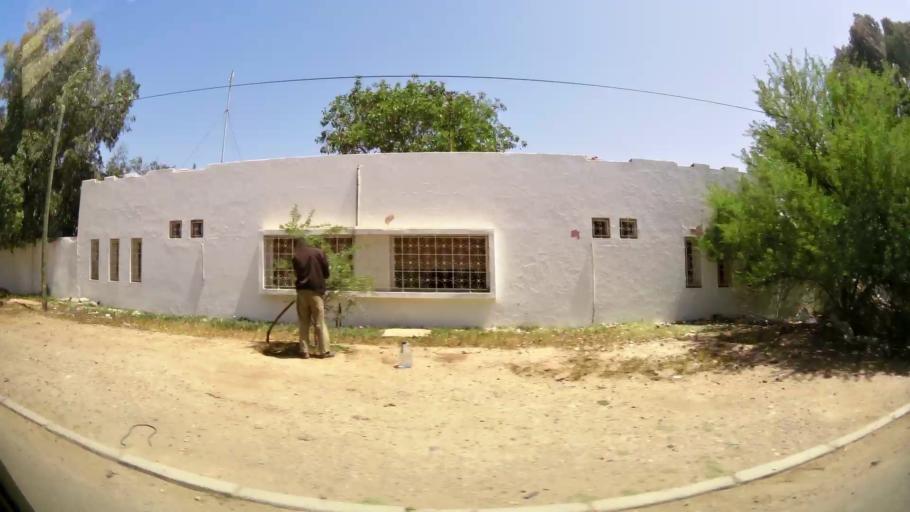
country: MA
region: Souss-Massa-Draa
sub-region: Inezgane-Ait Mellou
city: Inezgane
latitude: 30.3357
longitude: -9.4870
